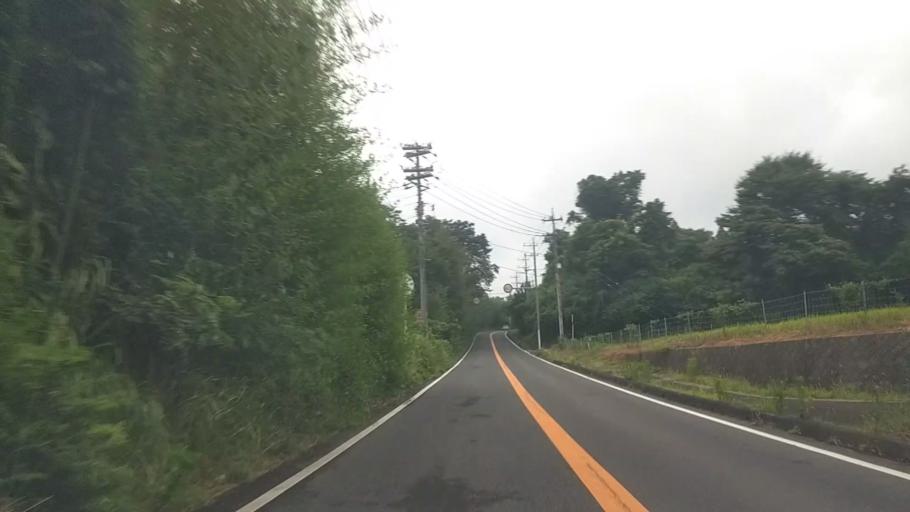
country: JP
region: Chiba
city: Kisarazu
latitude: 35.2801
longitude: 140.0776
